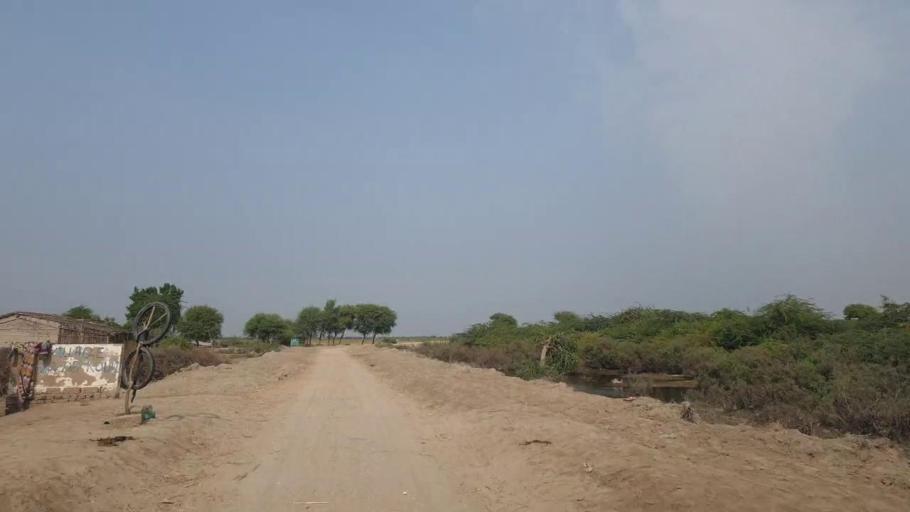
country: PK
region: Sindh
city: Badin
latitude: 24.6174
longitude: 68.7411
